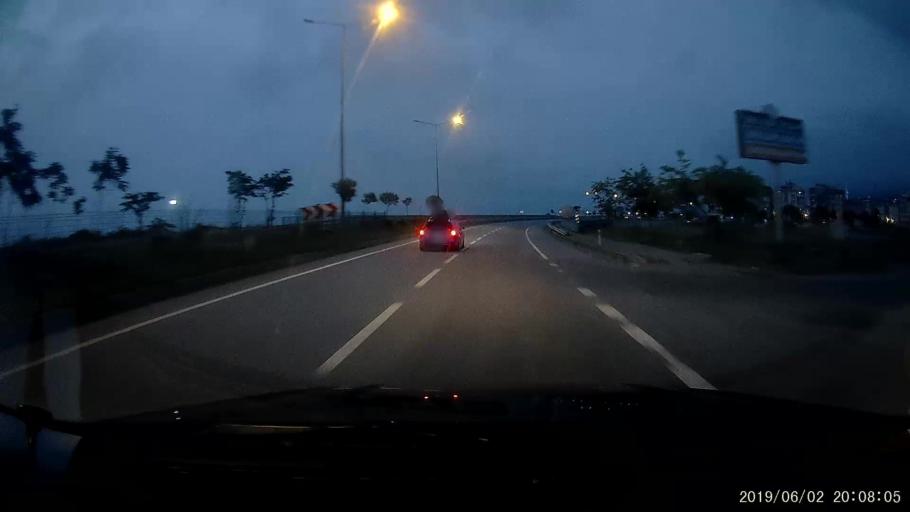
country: TR
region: Giresun
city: Gorele
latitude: 41.0376
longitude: 38.9916
